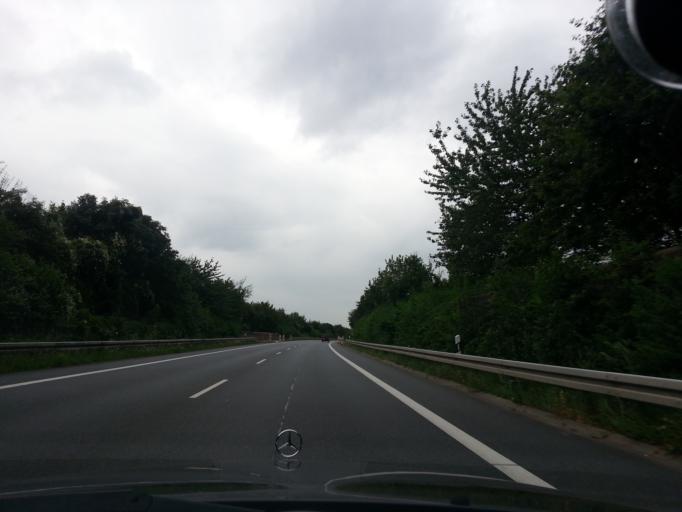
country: DE
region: North Rhine-Westphalia
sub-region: Regierungsbezirk Munster
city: Borken
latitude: 51.8351
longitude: 6.8413
